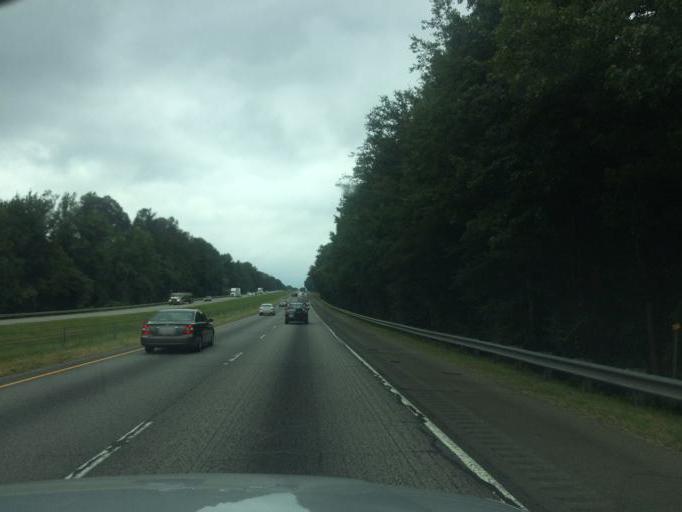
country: US
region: Georgia
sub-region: Franklin County
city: Carnesville
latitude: 34.3998
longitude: -83.2112
